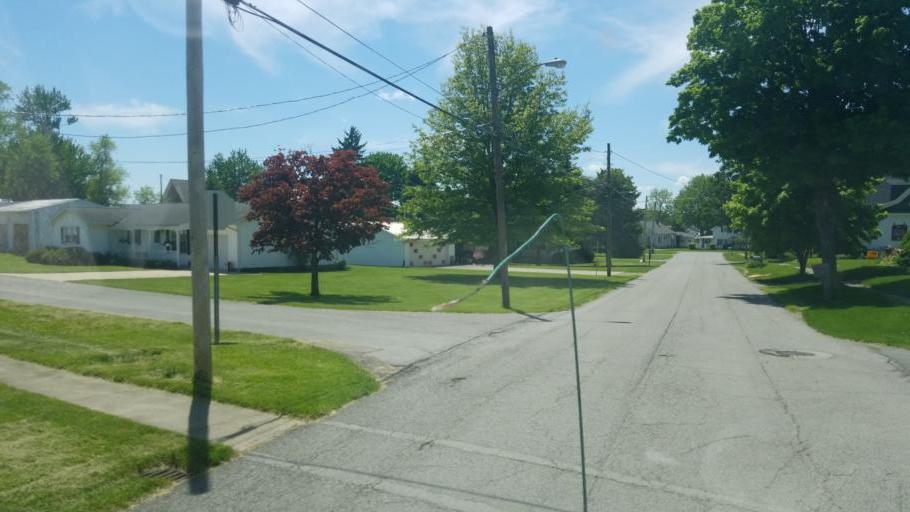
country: US
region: Ohio
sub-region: Huron County
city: Willard
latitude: 41.0664
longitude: -82.8848
